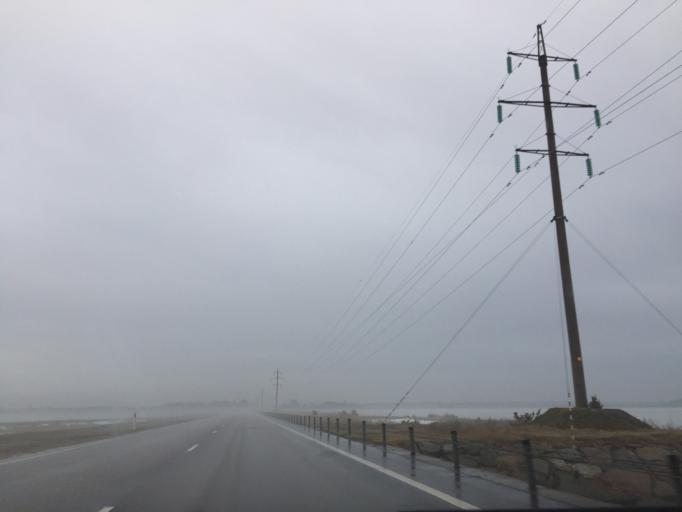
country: EE
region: Saare
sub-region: Orissaare vald
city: Orissaare
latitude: 58.5629
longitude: 23.1568
